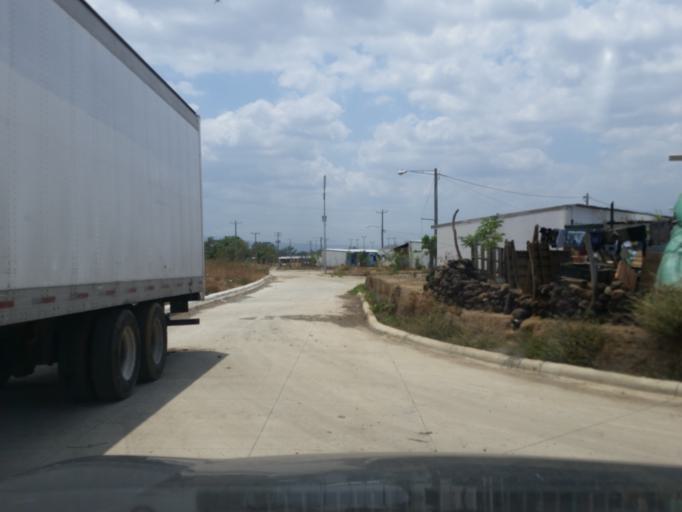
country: NI
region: Managua
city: Tipitapa
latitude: 12.1329
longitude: -86.1548
